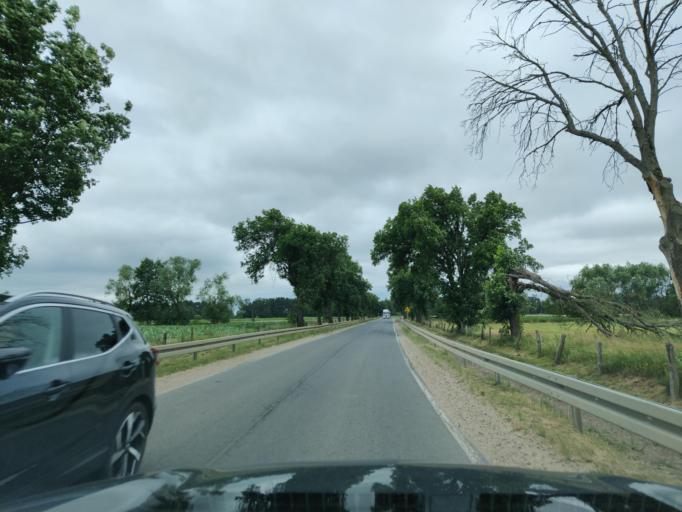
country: PL
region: Warmian-Masurian Voivodeship
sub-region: Powiat szczycienski
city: Wielbark
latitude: 53.3018
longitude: 21.0051
